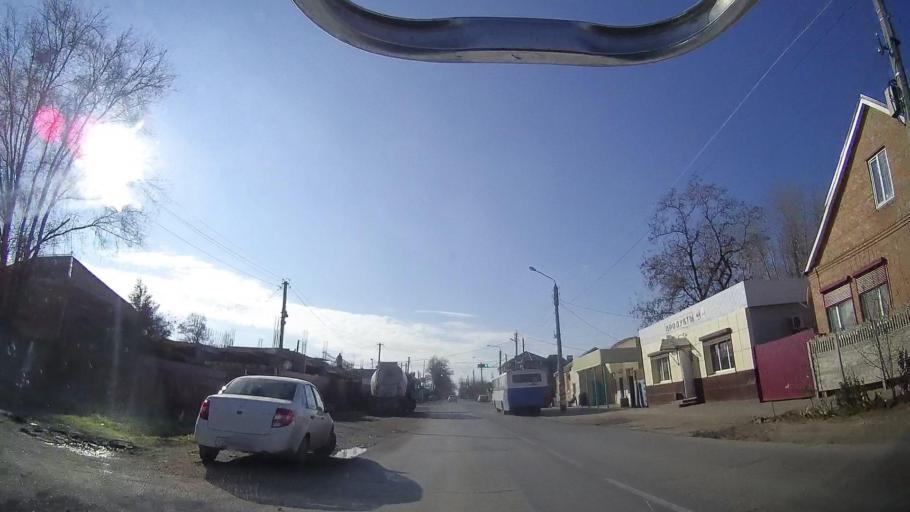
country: RU
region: Rostov
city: Bataysk
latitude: 47.1185
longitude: 39.6828
